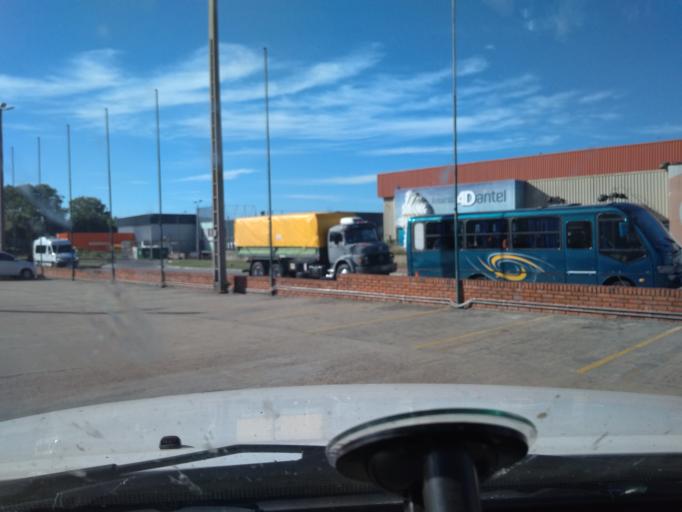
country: UY
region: Canelones
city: Paso de Carrasco
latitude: -34.8804
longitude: -56.0797
